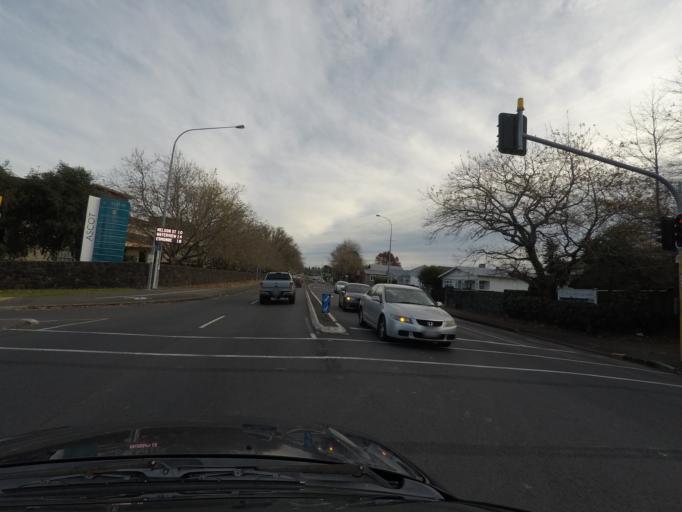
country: NZ
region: Auckland
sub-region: Auckland
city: Auckland
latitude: -36.8865
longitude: 174.8012
